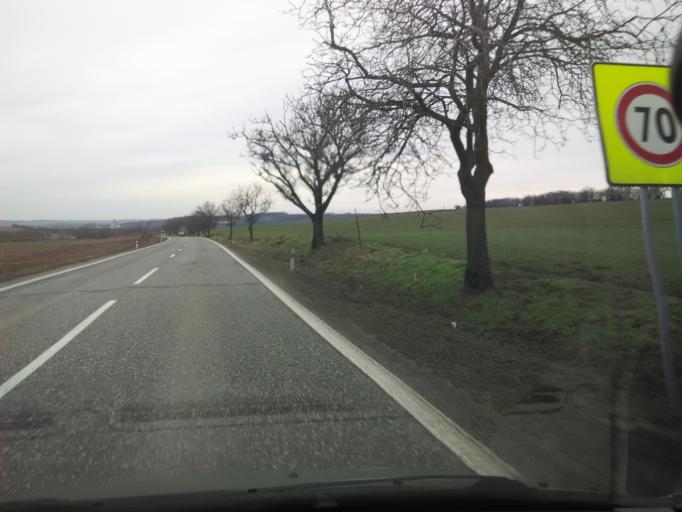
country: SK
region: Nitriansky
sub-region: Okres Nitra
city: Vrable
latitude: 48.2788
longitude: 18.2219
